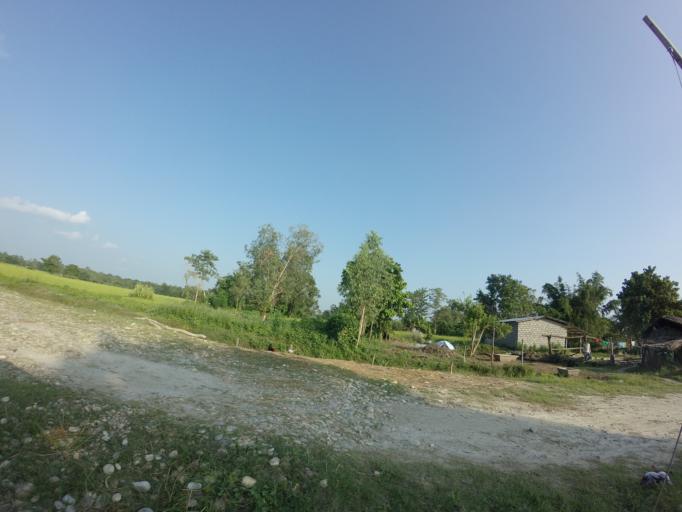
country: NP
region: Far Western
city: Tikapur
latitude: 28.4423
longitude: 81.0714
